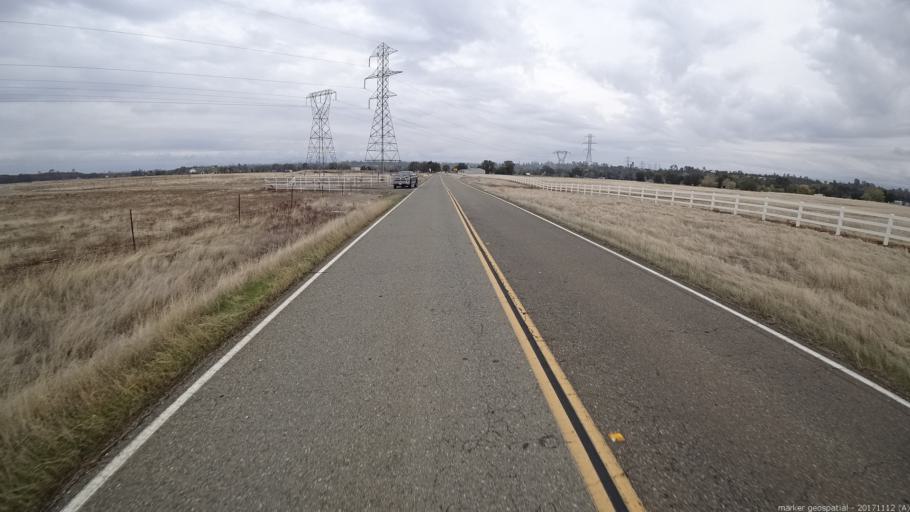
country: US
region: California
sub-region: Shasta County
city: Palo Cedro
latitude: 40.5357
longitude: -122.1740
